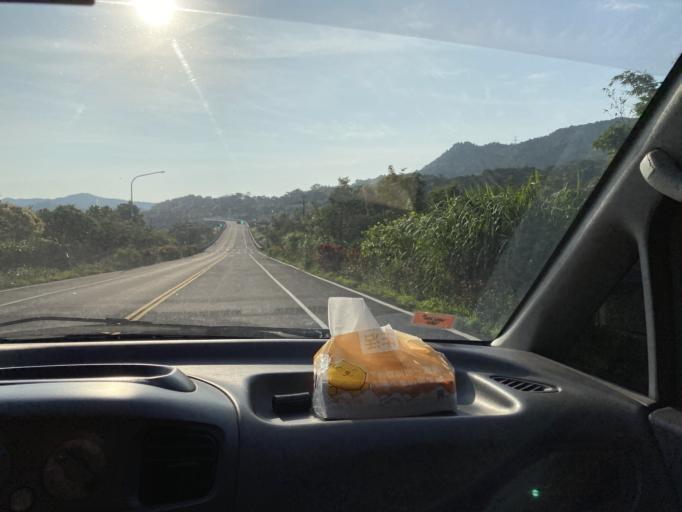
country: TW
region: Taiwan
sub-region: Keelung
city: Keelung
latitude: 25.0358
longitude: 121.8541
